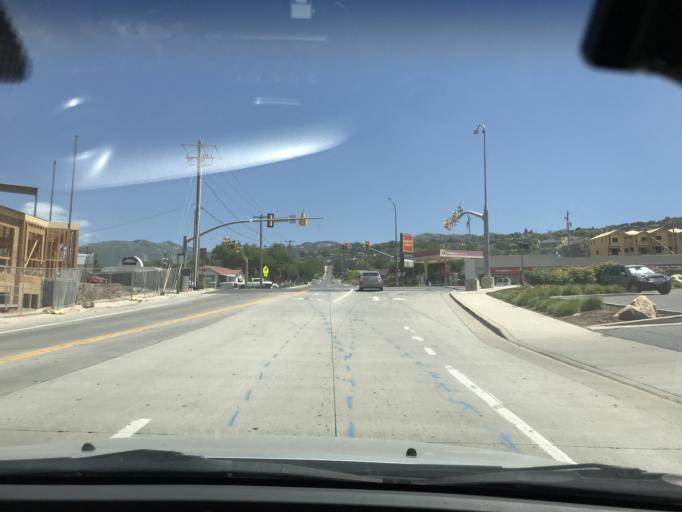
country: US
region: Utah
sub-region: Davis County
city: North Salt Lake
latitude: 40.8418
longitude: -111.9110
